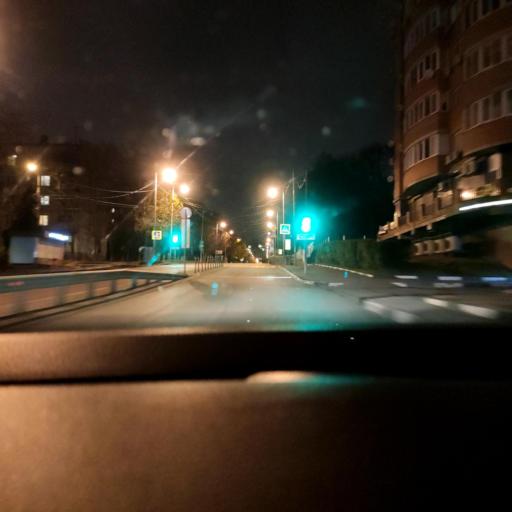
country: RU
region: Moskovskaya
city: Kotel'niki
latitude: 55.6318
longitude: 37.8478
